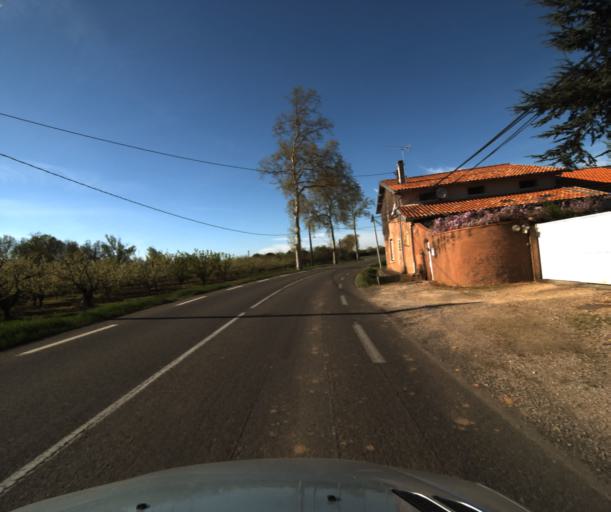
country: FR
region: Midi-Pyrenees
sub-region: Departement du Tarn-et-Garonne
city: Montbeton
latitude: 44.0469
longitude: 1.2982
